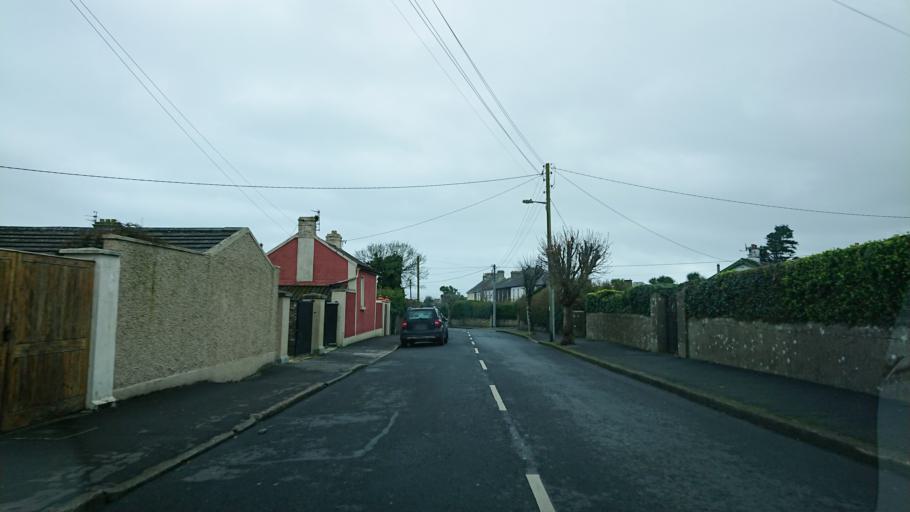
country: IE
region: Munster
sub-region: Waterford
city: Tra Mhor
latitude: 52.1621
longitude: -7.1554
